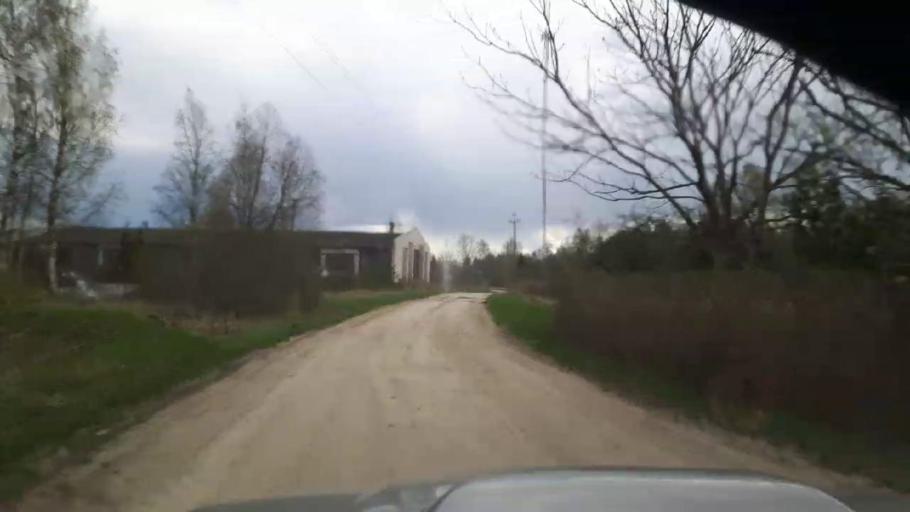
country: EE
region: Paernumaa
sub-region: Tootsi vald
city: Tootsi
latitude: 58.5203
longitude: 24.8168
